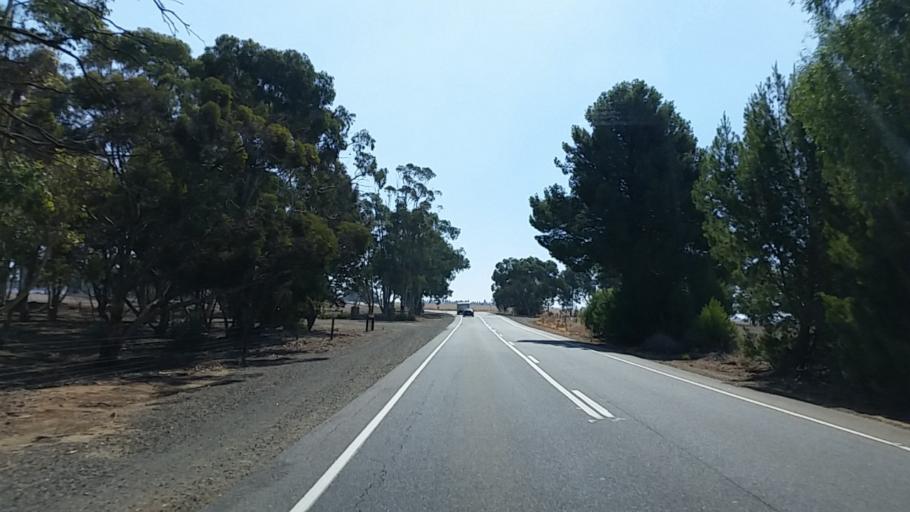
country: AU
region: South Australia
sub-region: Light
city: Kapunda
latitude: -34.2369
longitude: 138.7427
